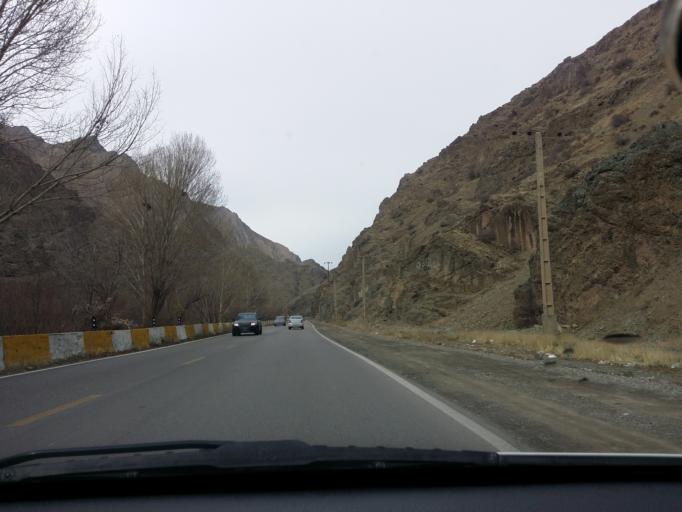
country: IR
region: Tehran
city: Tajrish
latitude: 36.0139
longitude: 51.2895
